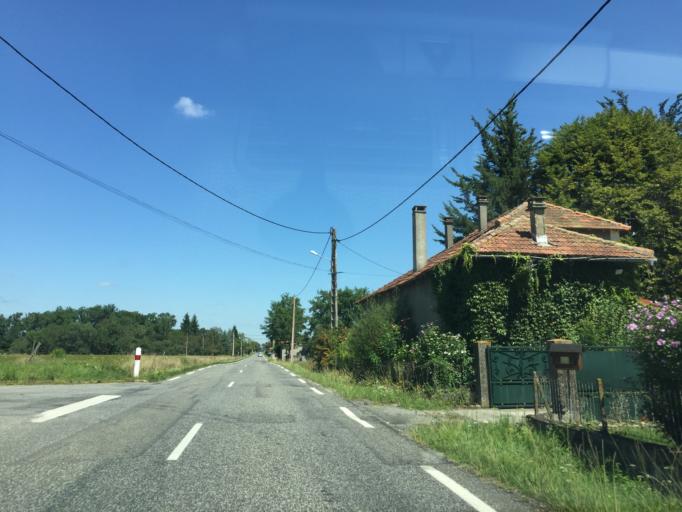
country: FR
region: Midi-Pyrenees
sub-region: Departement des Hautes-Pyrenees
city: Trie-sur-Baise
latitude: 43.2597
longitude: 0.4296
